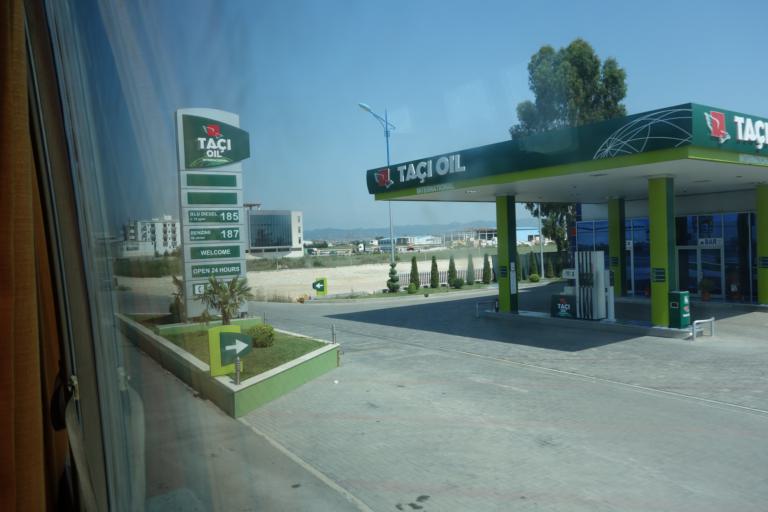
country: AL
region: Durres
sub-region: Rrethi i Durresit
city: Rrashbull
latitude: 41.3458
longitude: 19.5047
